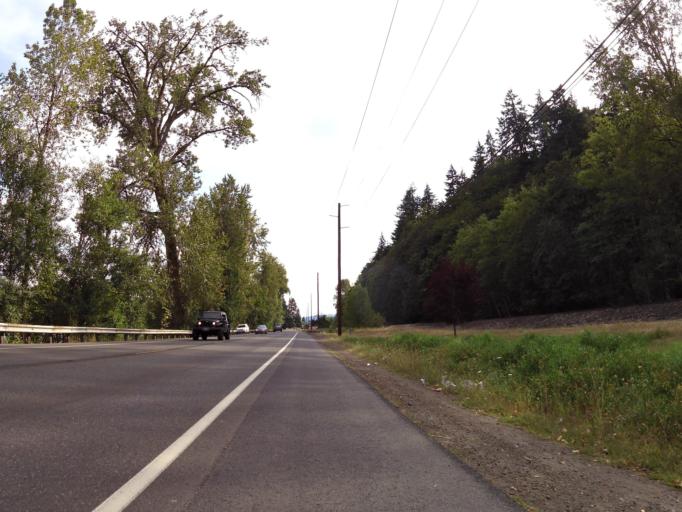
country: US
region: Washington
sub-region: Cowlitz County
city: Kelso
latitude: 46.1582
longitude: -122.9158
